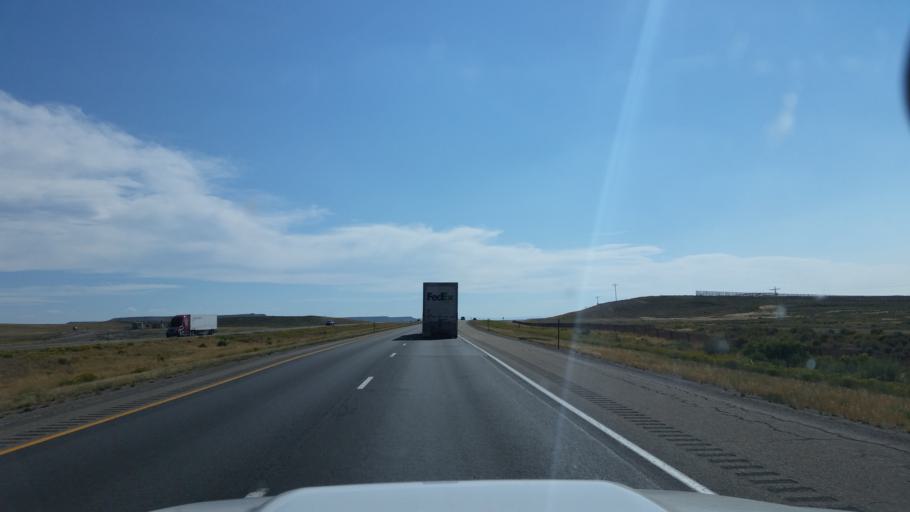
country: US
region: Wyoming
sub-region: Uinta County
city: Lyman
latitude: 41.4709
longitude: -110.0392
